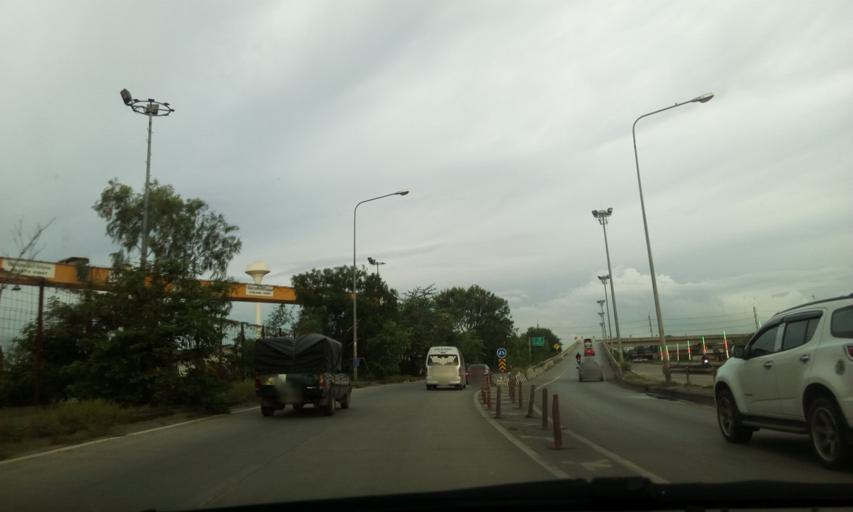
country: TH
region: Phra Nakhon Si Ayutthaya
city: Ban Bang Kadi Pathum Thani
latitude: 13.9714
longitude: 100.5536
